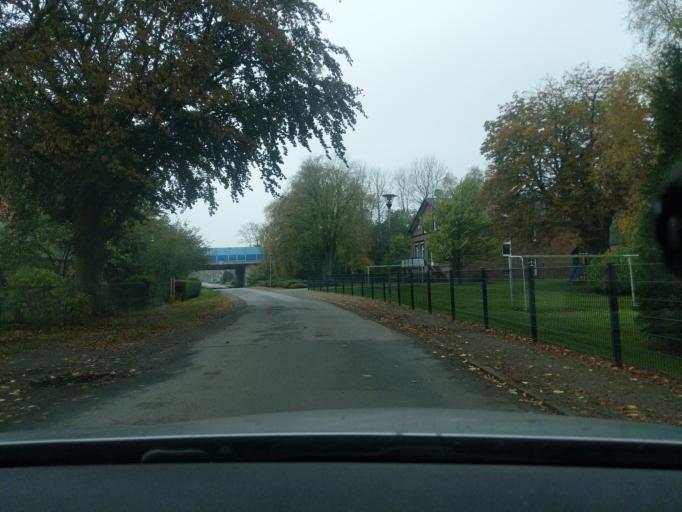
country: DE
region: Lower Saxony
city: Cuxhaven
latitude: 53.8393
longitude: 8.7347
